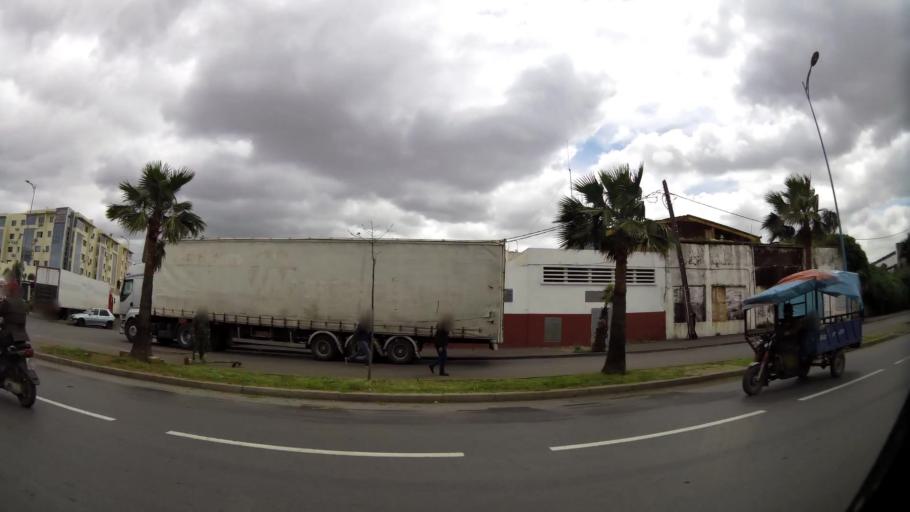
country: MA
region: Grand Casablanca
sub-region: Casablanca
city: Casablanca
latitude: 33.5934
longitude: -7.5457
